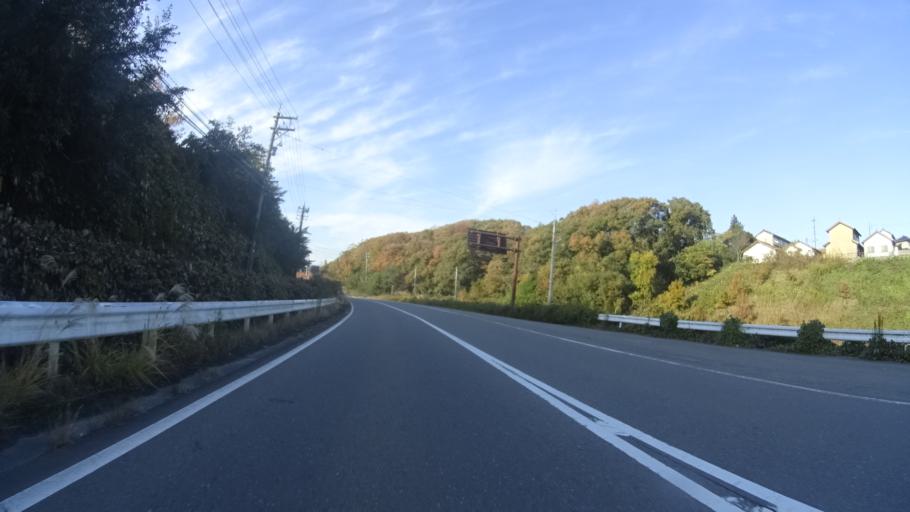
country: JP
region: Ishikawa
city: Hakui
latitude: 37.0236
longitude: 136.7857
